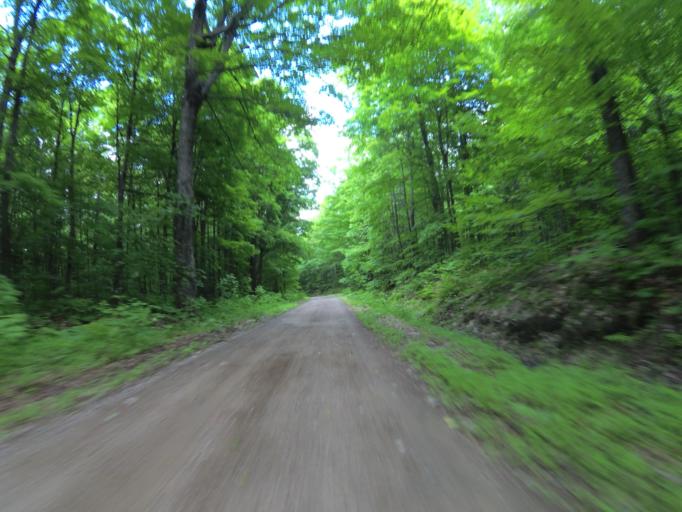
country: CA
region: Ontario
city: Renfrew
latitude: 45.1362
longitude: -76.8781
